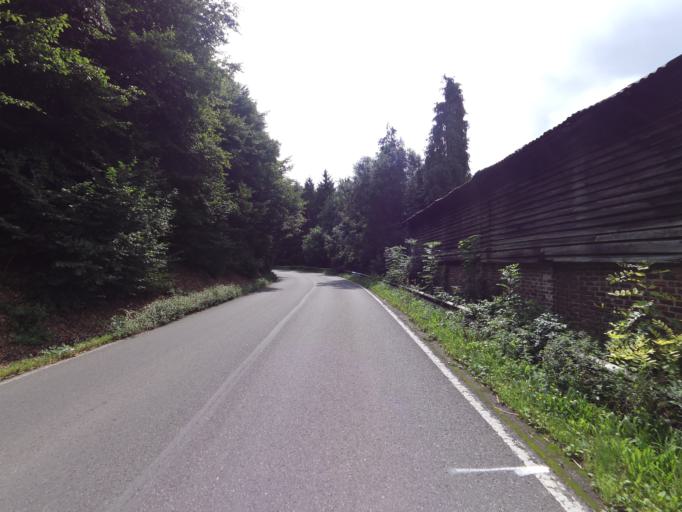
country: BE
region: Wallonia
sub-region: Province de Liege
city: Amay
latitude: 50.5408
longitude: 5.3435
